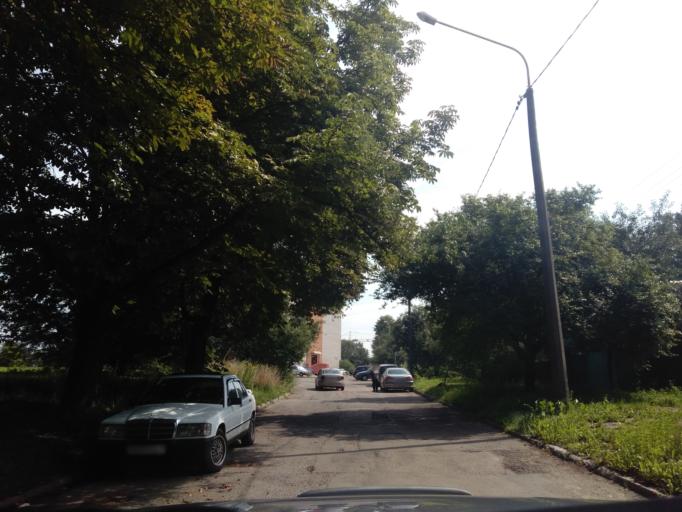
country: BY
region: Minsk
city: Novoye Medvezhino
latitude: 53.8817
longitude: 27.4946
